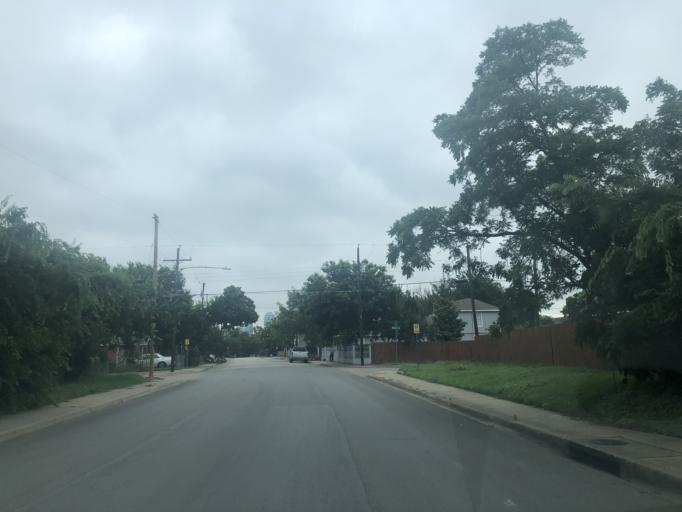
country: US
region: Texas
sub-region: Dallas County
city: Dallas
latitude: 32.7817
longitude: -96.8454
